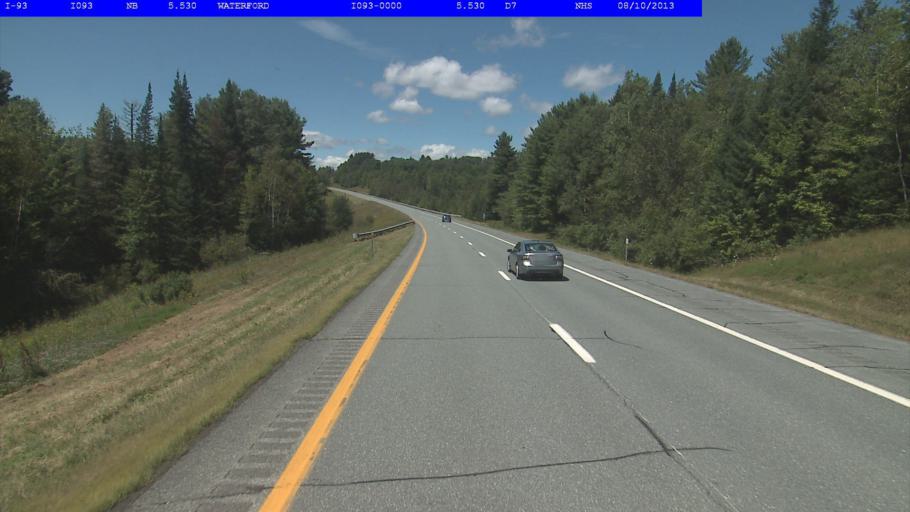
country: US
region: Vermont
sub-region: Caledonia County
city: Saint Johnsbury
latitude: 44.4145
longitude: -71.9232
